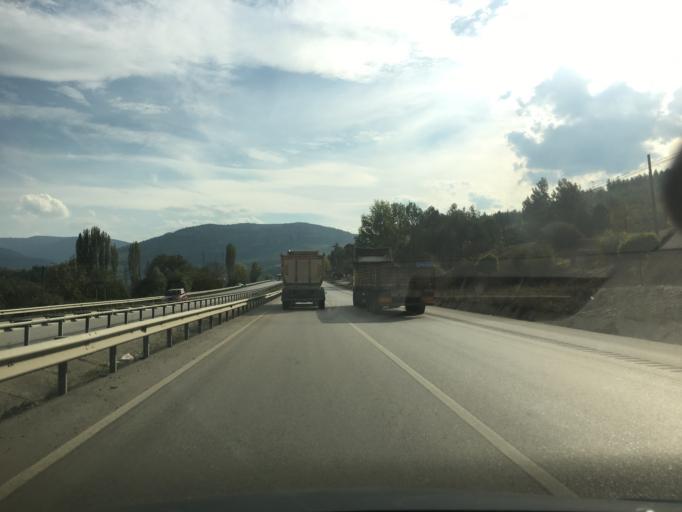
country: TR
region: Karabuk
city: Karabuk
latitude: 41.1150
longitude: 32.6715
